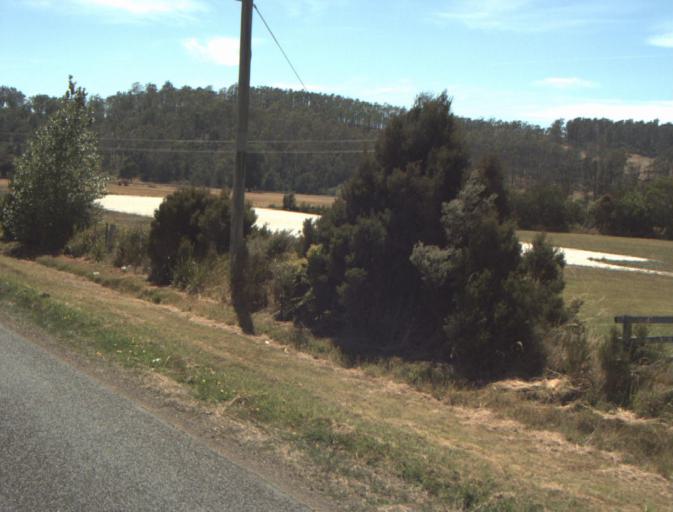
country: AU
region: Tasmania
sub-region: Launceston
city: Mayfield
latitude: -41.2539
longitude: 147.1470
